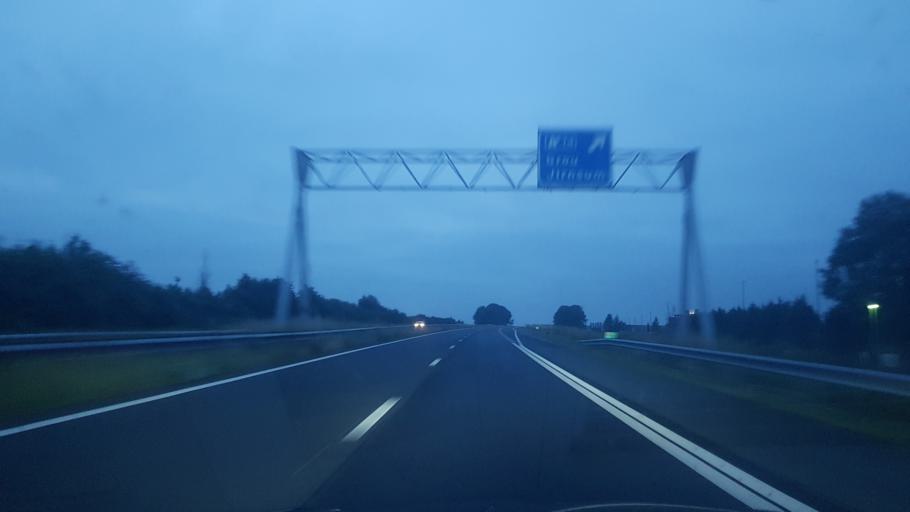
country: NL
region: Friesland
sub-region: Gemeente Boarnsterhim
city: Grou
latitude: 53.0838
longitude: 5.8266
